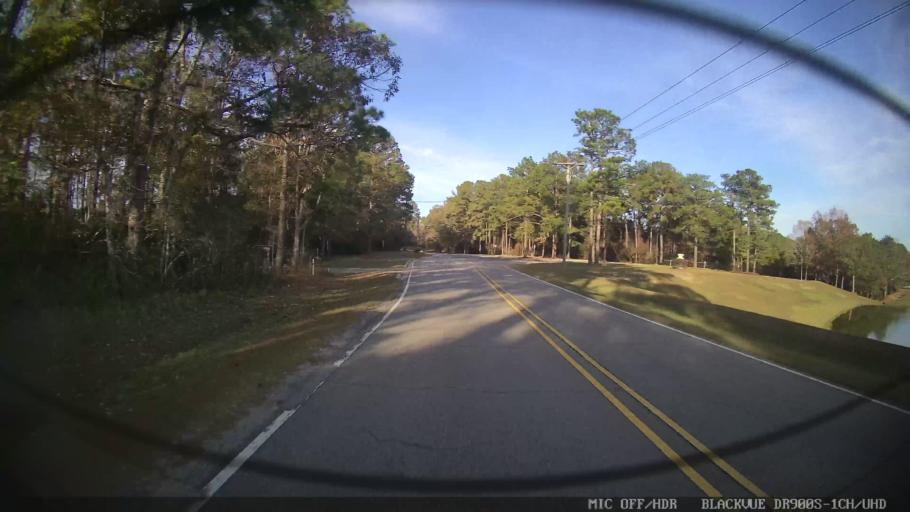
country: US
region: Mississippi
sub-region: Forrest County
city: Hattiesburg
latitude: 31.2315
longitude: -89.3032
